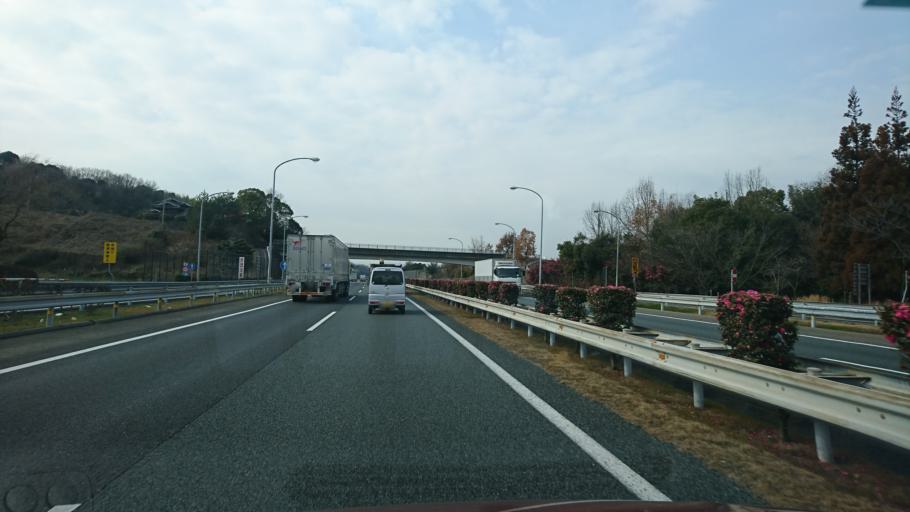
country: JP
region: Hiroshima
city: Kannabecho-yahiro
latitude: 34.5357
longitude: 133.4572
